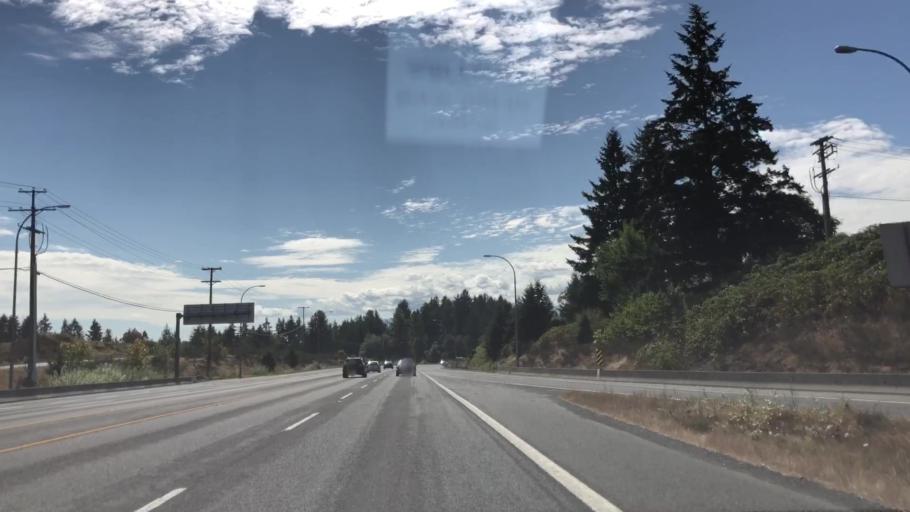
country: CA
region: British Columbia
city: Nanaimo
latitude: 49.1231
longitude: -123.8632
